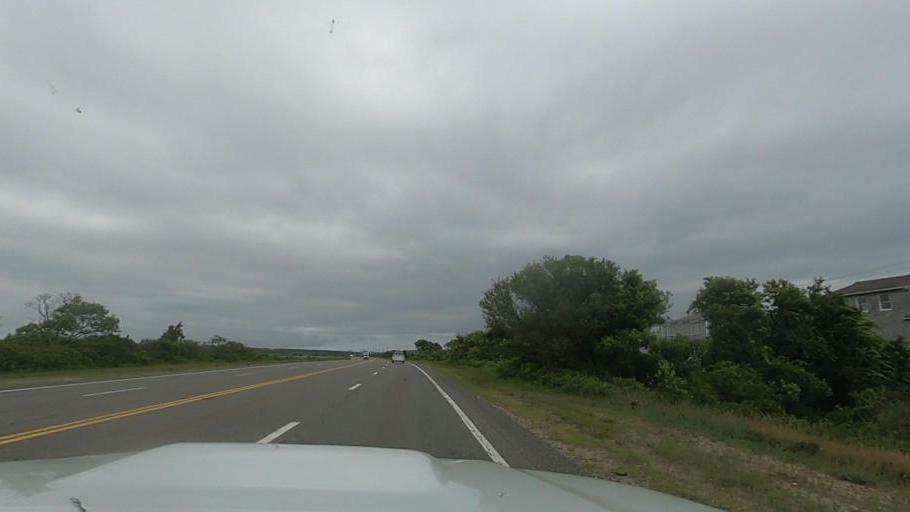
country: US
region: Massachusetts
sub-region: Barnstable County
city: Provincetown
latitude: 42.0586
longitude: -70.1374
